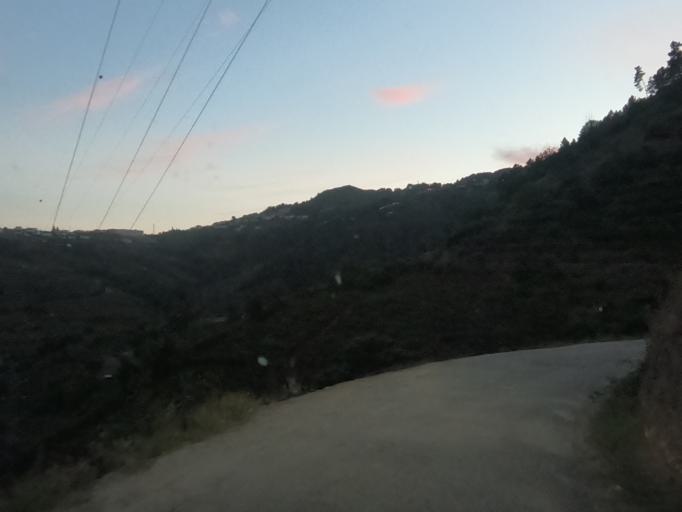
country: PT
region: Vila Real
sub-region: Vila Real
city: Vila Real
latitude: 41.2724
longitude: -7.7621
